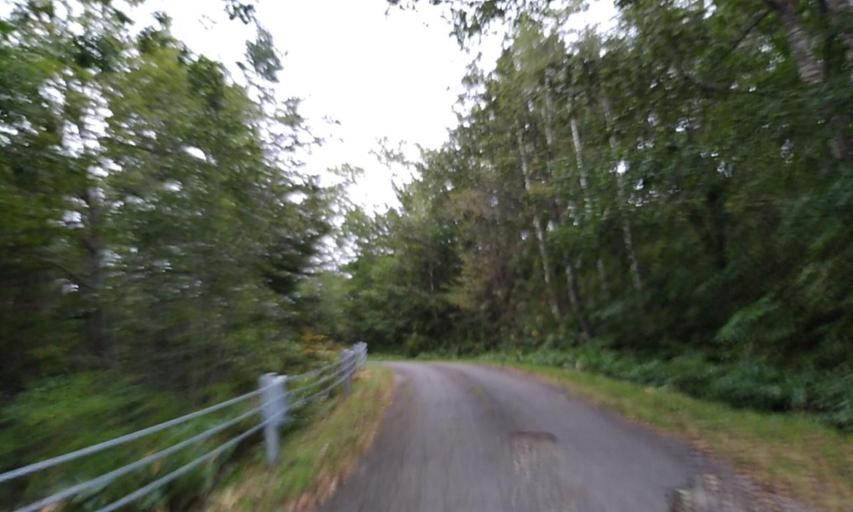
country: JP
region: Hokkaido
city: Obihiro
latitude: 42.8280
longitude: 142.9822
